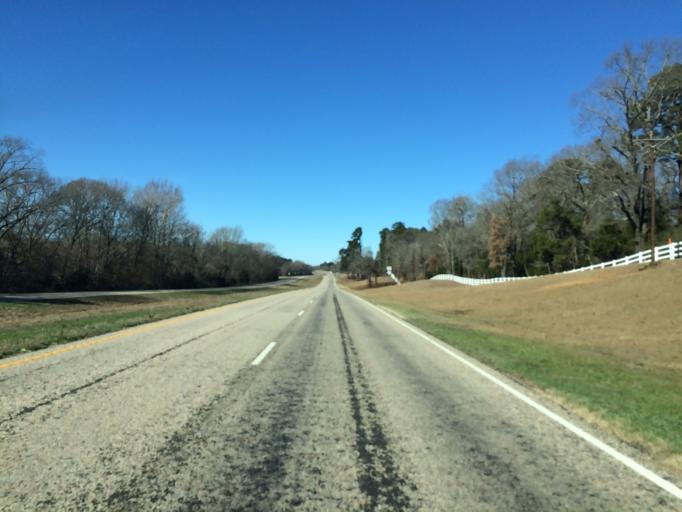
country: US
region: Texas
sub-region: Wood County
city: Mineola
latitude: 32.6468
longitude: -95.4109
